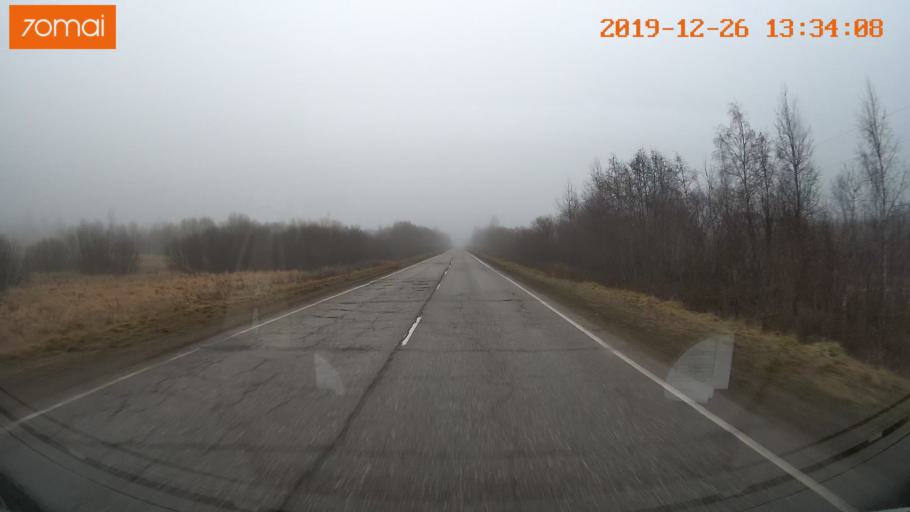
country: RU
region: Vologda
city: Sheksna
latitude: 58.8093
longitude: 38.3186
